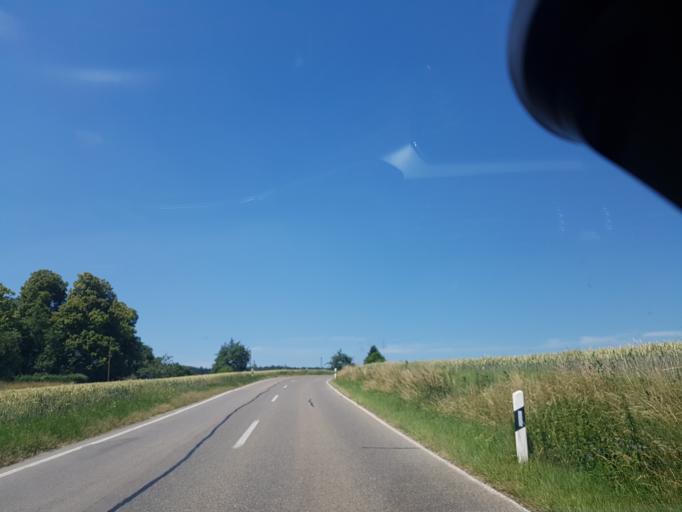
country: DE
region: Baden-Wuerttemberg
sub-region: Tuebingen Region
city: Blaubeuren
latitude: 48.4224
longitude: 9.8678
